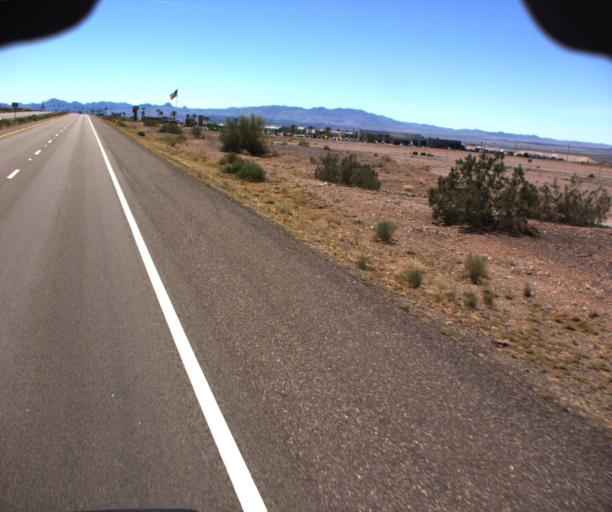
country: US
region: Arizona
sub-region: Mohave County
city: Desert Hills
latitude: 34.5781
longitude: -114.3667
